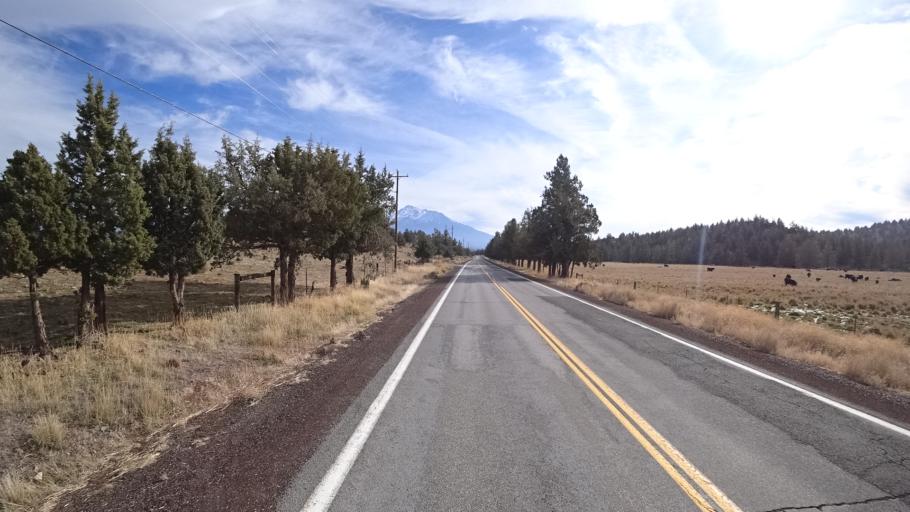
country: US
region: California
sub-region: Siskiyou County
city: Weed
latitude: 41.5801
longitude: -122.3983
